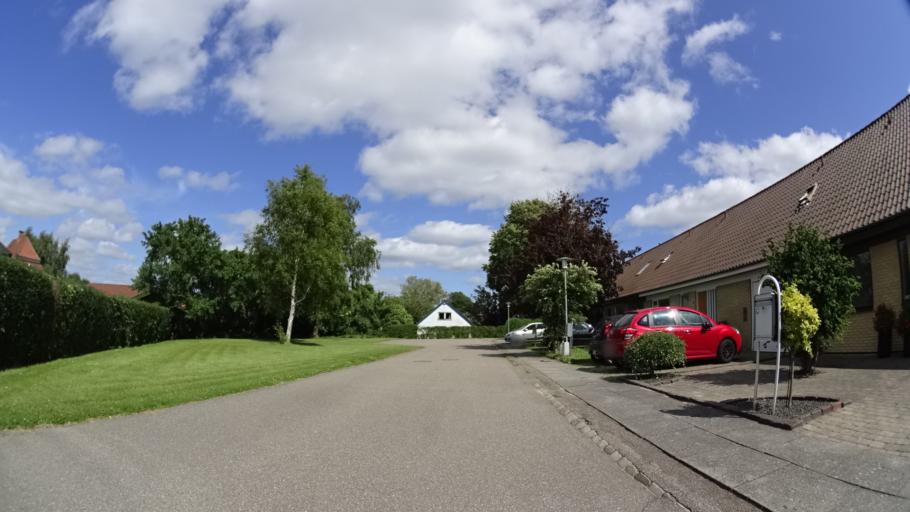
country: DK
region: Central Jutland
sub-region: Arhus Kommune
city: Stavtrup
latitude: 56.1452
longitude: 10.1585
